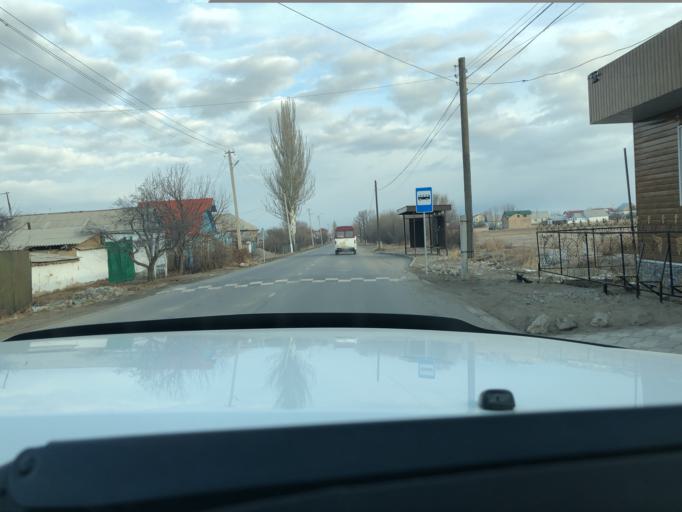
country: KG
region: Ysyk-Koel
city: Karakol
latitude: 42.4683
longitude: 78.3731
